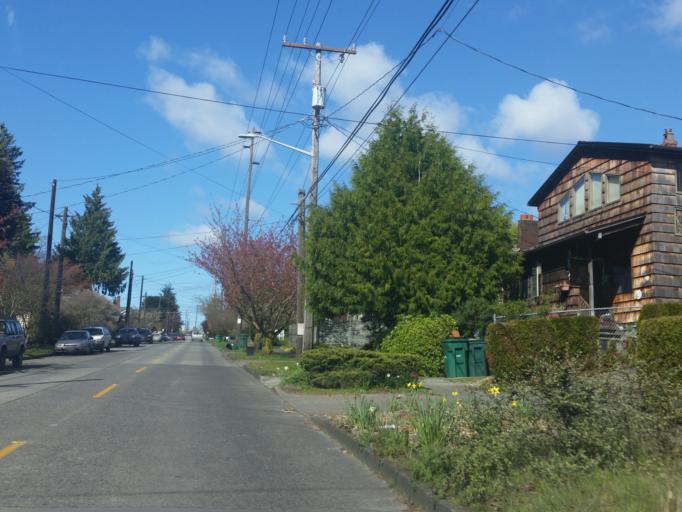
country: US
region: Washington
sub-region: King County
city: Seattle
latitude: 47.6782
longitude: -122.3605
